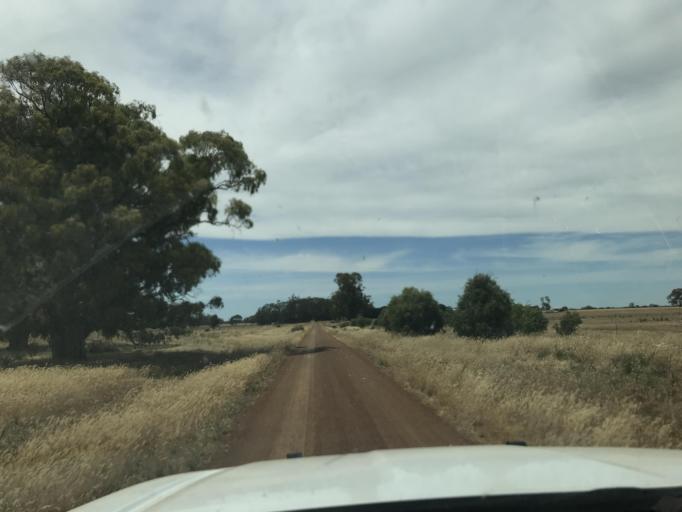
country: AU
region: South Australia
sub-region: Wattle Range
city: Penola
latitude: -37.0248
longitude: 141.4889
